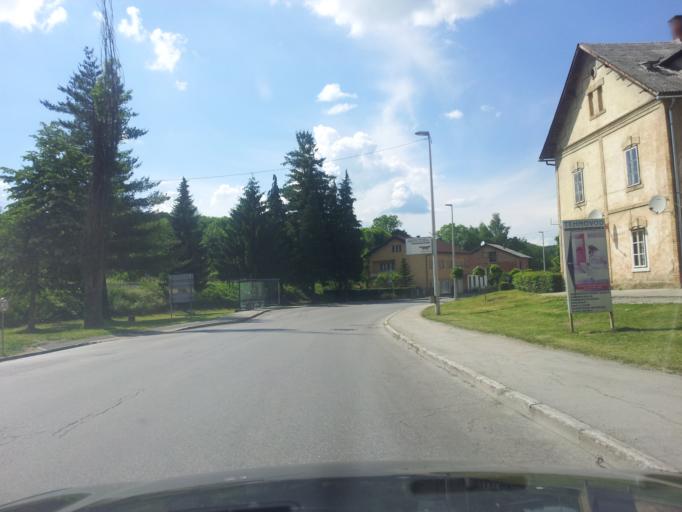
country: HR
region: Karlovacka
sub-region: Grad Karlovac
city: Karlovac
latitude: 45.4510
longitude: 15.4971
